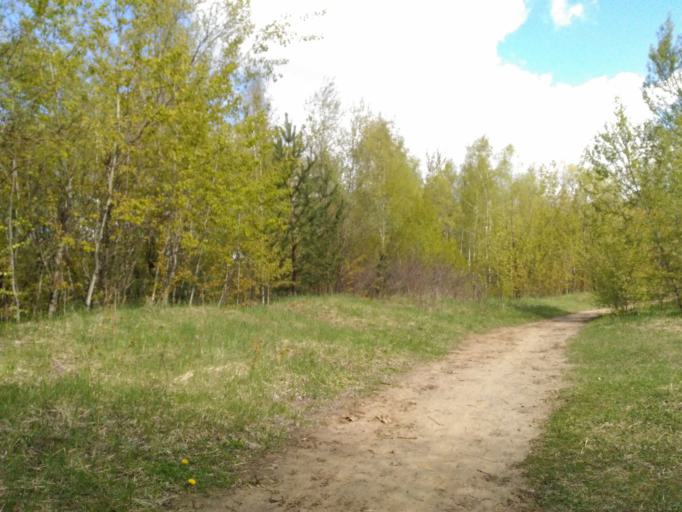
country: RU
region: Moscow
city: Shchukino
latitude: 55.7771
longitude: 37.4339
